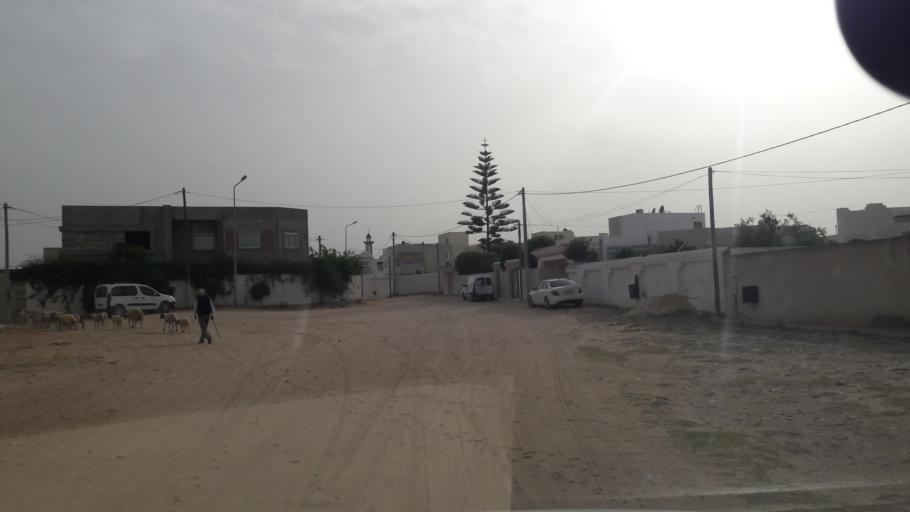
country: TN
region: Safaqis
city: Al Qarmadah
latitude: 34.7802
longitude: 10.7728
